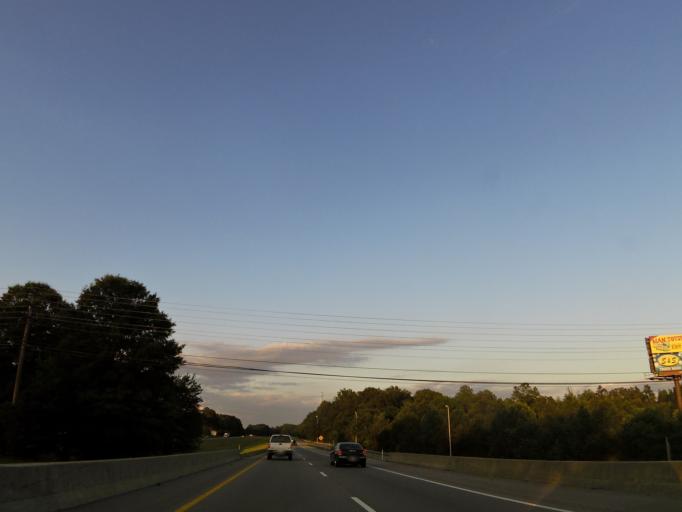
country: US
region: Tennessee
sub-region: Putnam County
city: Baxter
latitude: 36.1374
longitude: -85.6291
